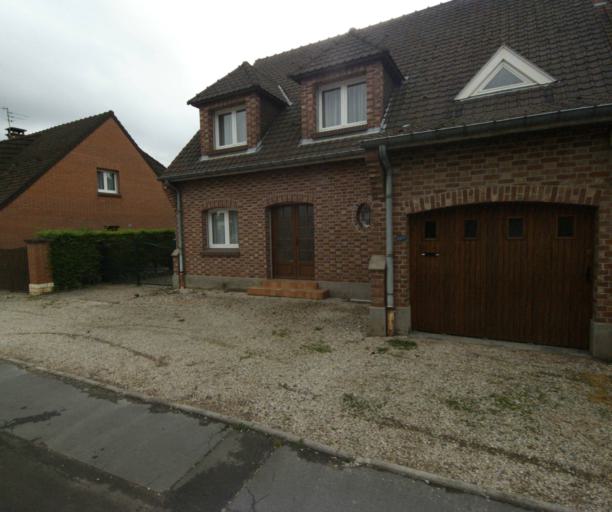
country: FR
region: Nord-Pas-de-Calais
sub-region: Departement du Nord
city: Wavrin
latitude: 50.5727
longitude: 2.9438
